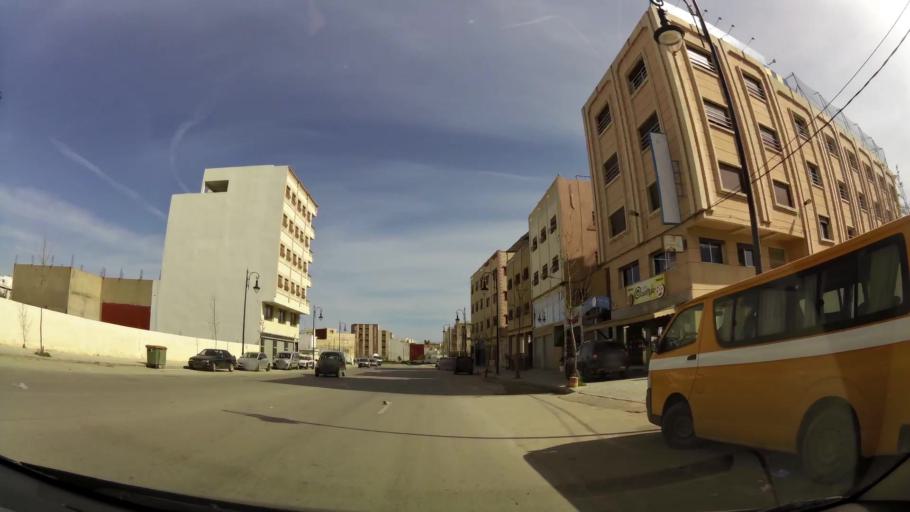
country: MA
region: Tanger-Tetouan
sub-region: Tanger-Assilah
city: Tangier
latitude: 35.7204
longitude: -5.8045
